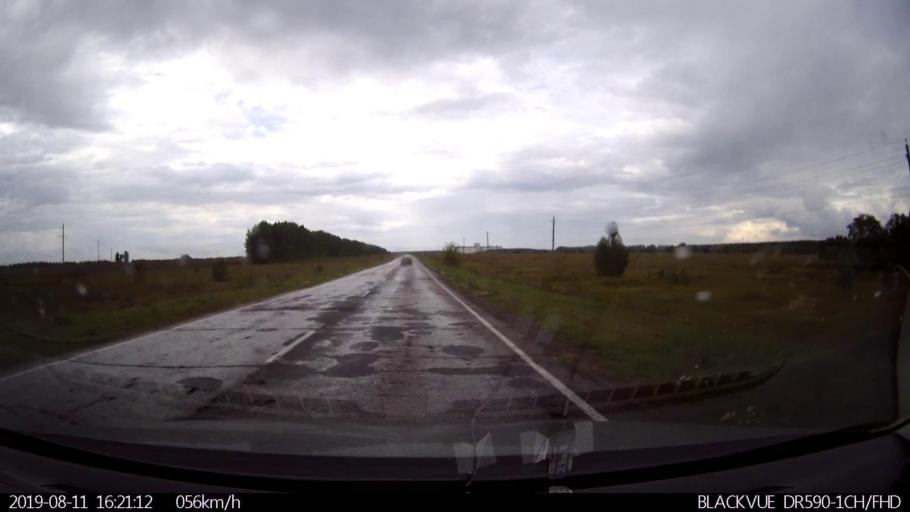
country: RU
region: Ulyanovsk
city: Mayna
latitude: 54.0780
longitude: 47.5991
